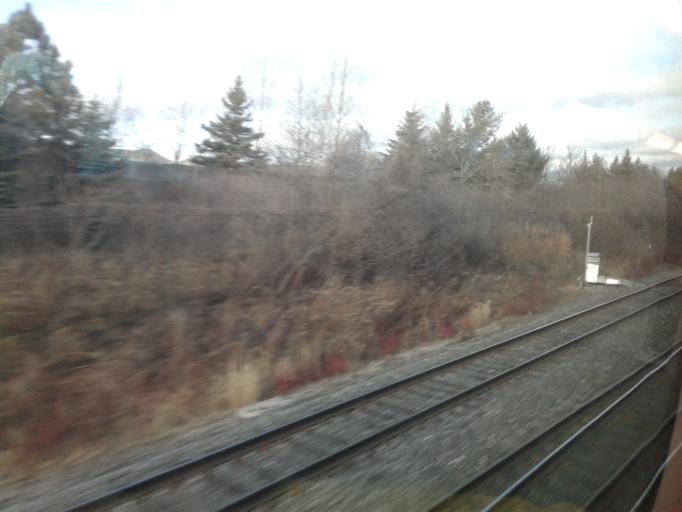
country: CA
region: Ontario
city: Mississauga
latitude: 43.5453
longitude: -79.5990
